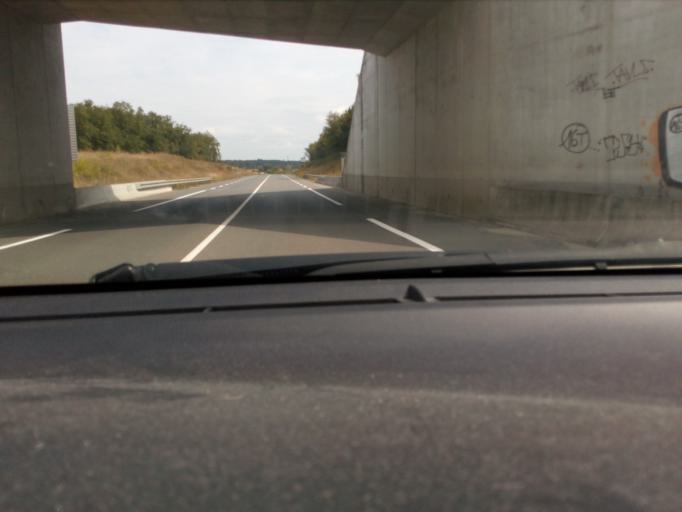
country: FR
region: Poitou-Charentes
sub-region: Departement de la Charente
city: Saint-Saturnin
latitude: 45.6802
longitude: 0.0745
